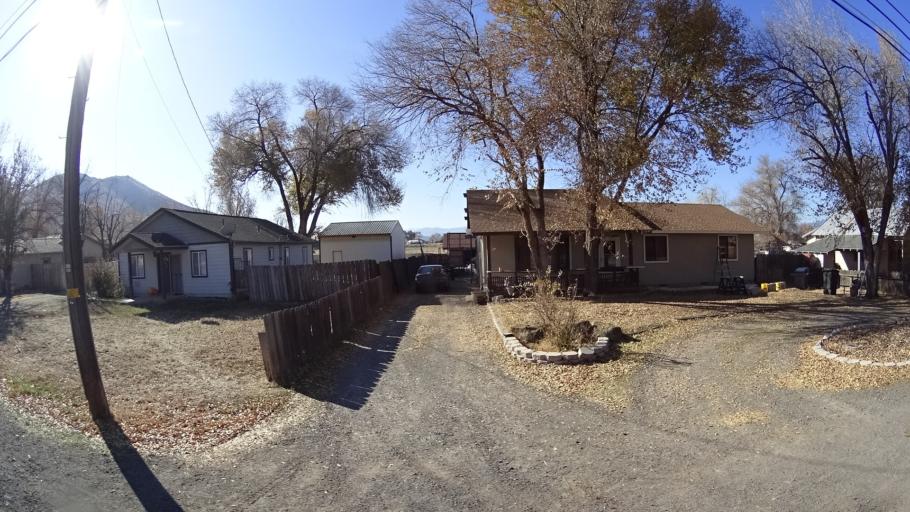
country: US
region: California
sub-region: Siskiyou County
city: Montague
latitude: 41.7251
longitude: -122.5198
